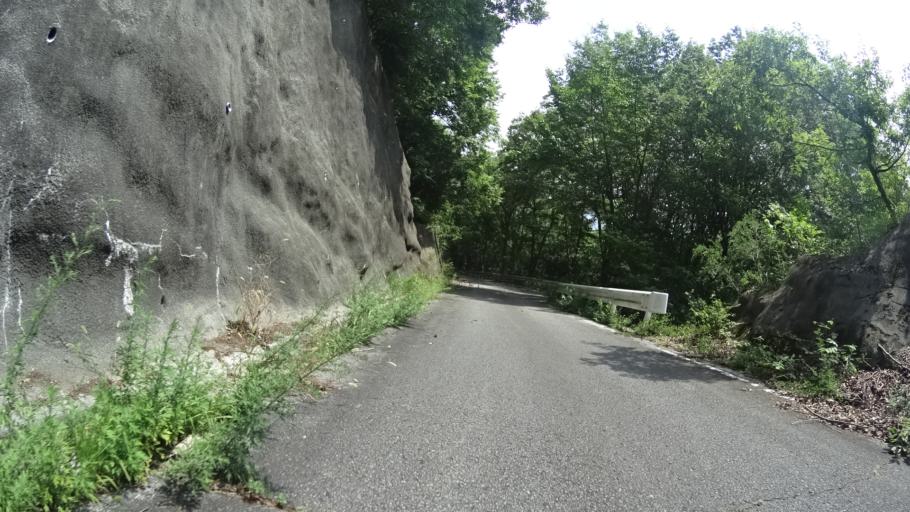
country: JP
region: Yamanashi
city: Nirasaki
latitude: 35.8802
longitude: 138.4989
